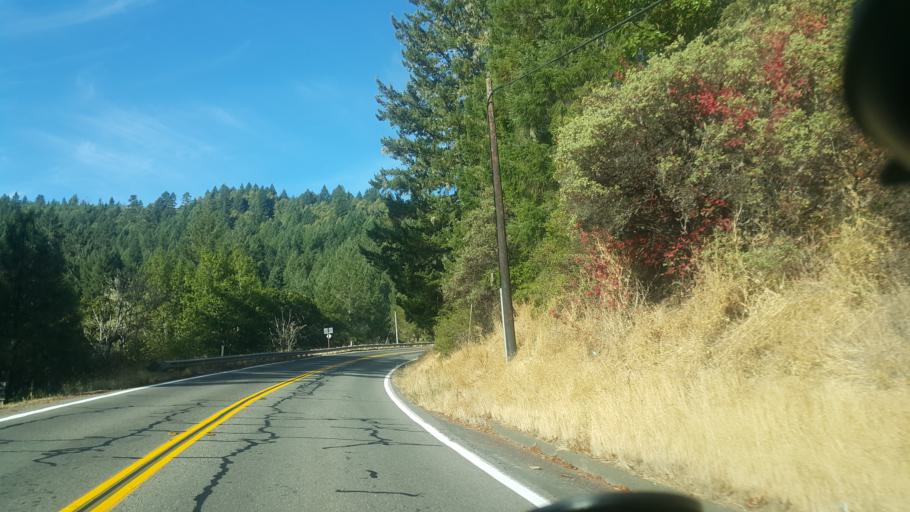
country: US
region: California
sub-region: Mendocino County
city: Brooktrails
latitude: 39.3878
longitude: -123.4269
